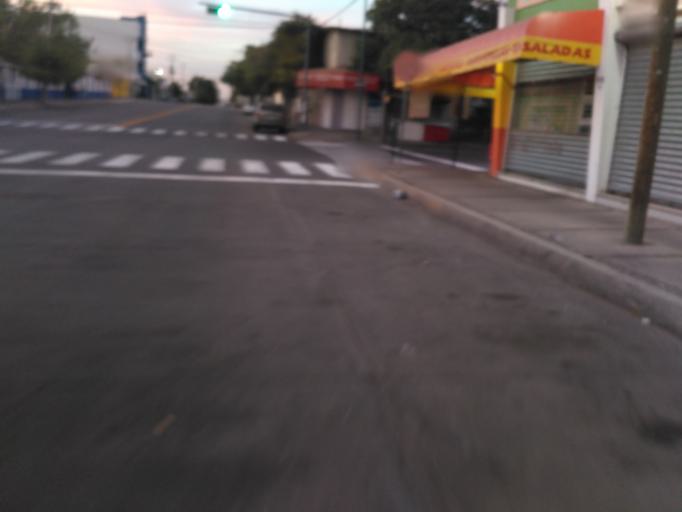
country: MX
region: Sinaloa
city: Culiacan
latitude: 24.8009
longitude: -107.4040
